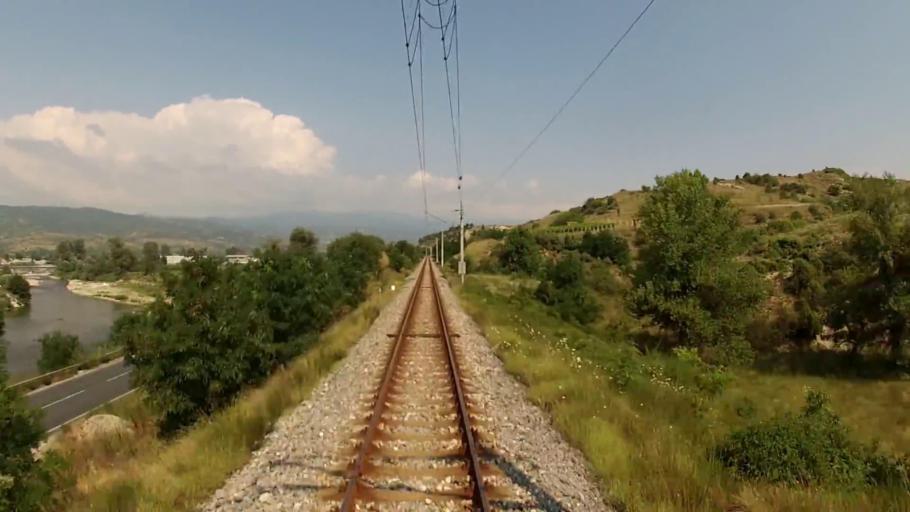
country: BG
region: Blagoevgrad
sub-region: Obshtina Strumyani
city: Strumyani
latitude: 41.6228
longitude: 23.2162
